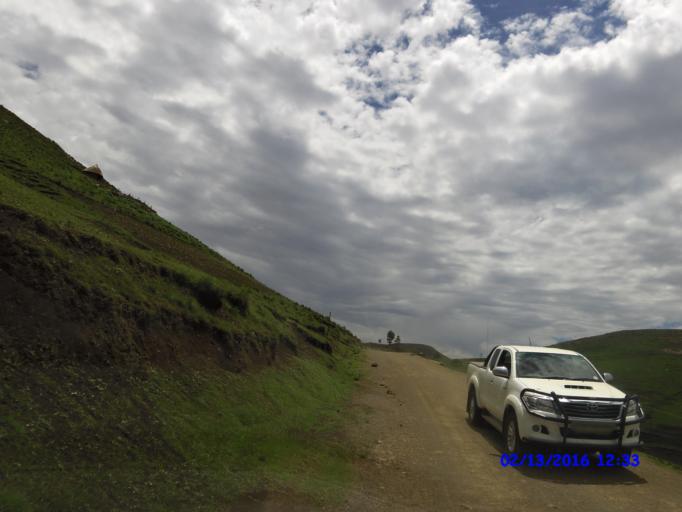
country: LS
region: Maseru
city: Nako
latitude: -29.8505
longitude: 28.0284
